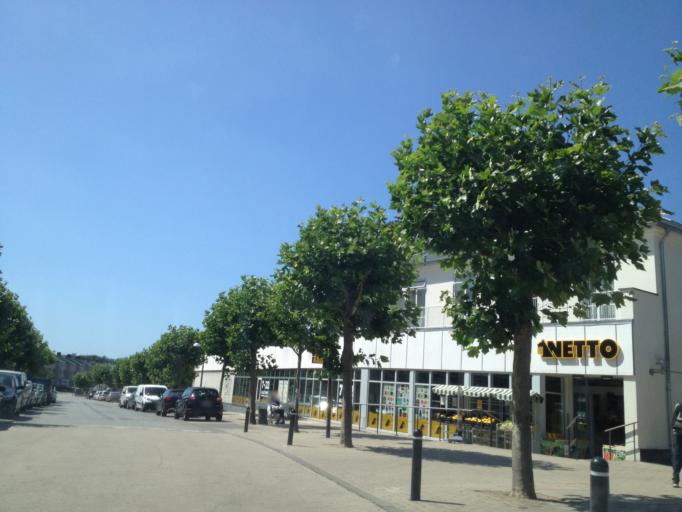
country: DK
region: Capital Region
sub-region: Rudersdal Kommune
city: Trorod
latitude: 55.8203
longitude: 12.5395
